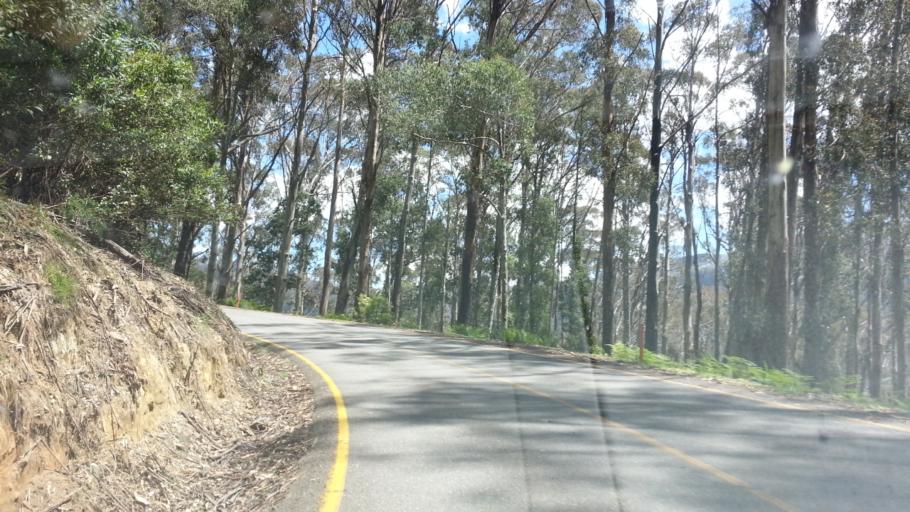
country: AU
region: Victoria
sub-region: Alpine
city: Mount Beauty
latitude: -36.8447
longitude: 147.2397
